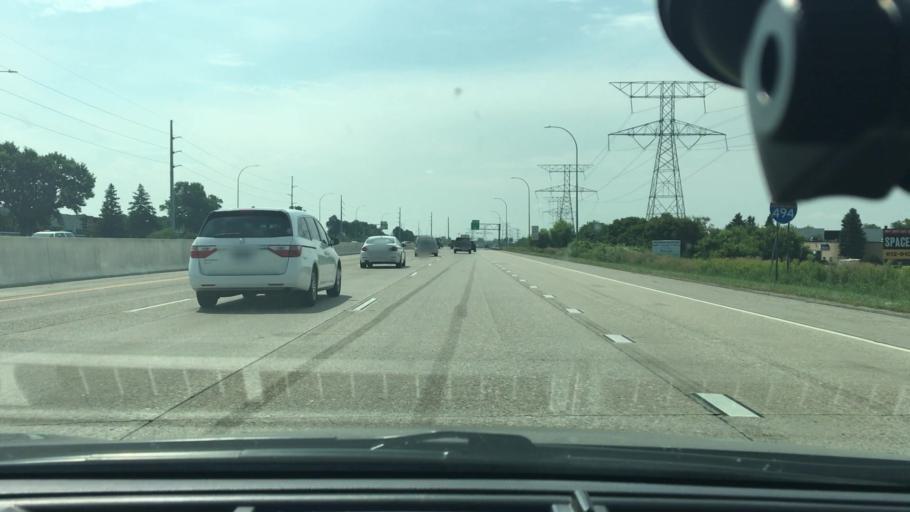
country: US
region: Minnesota
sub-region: Hennepin County
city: Plymouth
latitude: 45.0062
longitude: -93.4575
